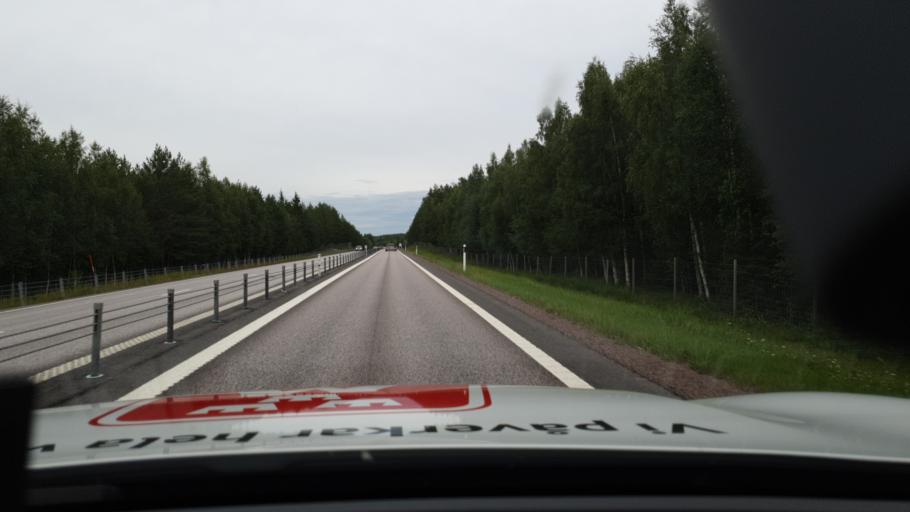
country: SE
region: Norrbotten
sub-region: Pitea Kommun
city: Rosvik
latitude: 65.4842
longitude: 21.7467
